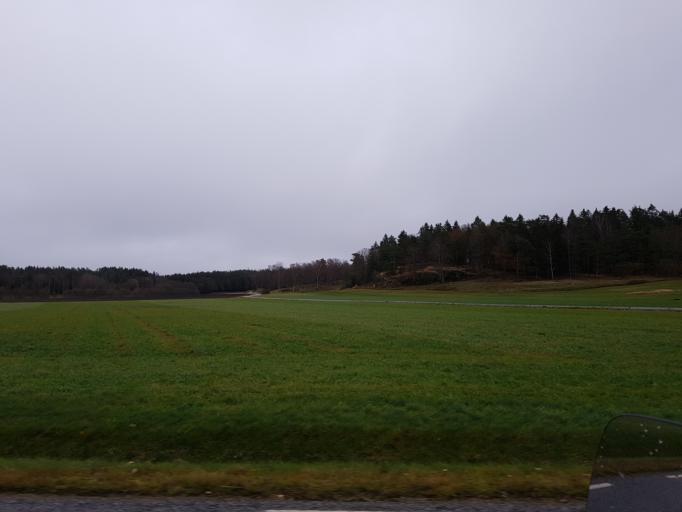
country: SE
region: Vaestra Goetaland
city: Svanesund
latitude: 58.1724
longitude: 11.7834
